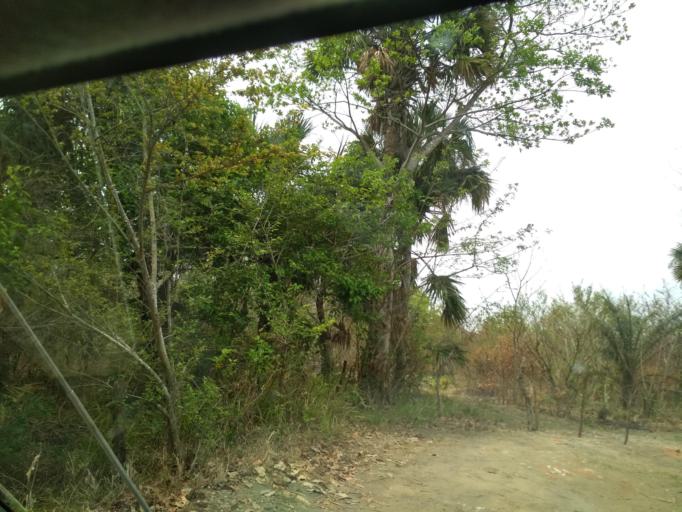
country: MX
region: Veracruz
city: Paso del Toro
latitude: 19.0222
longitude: -96.1417
